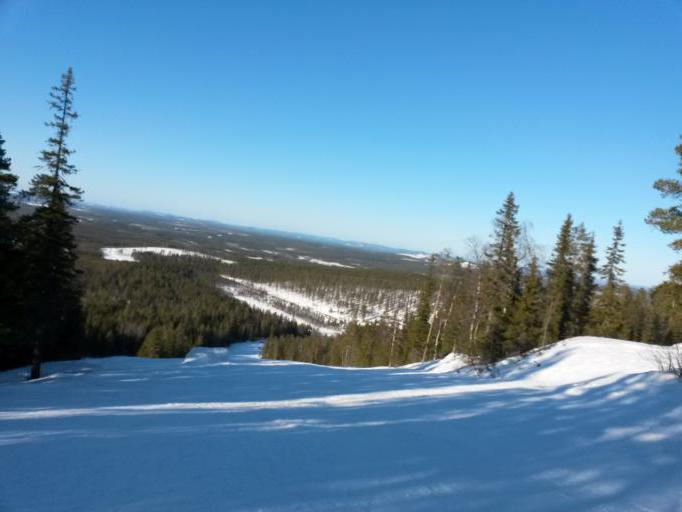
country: SE
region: Vaesterbotten
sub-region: Skelleftea Kommun
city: Langsele
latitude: 65.1558
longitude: 20.1338
